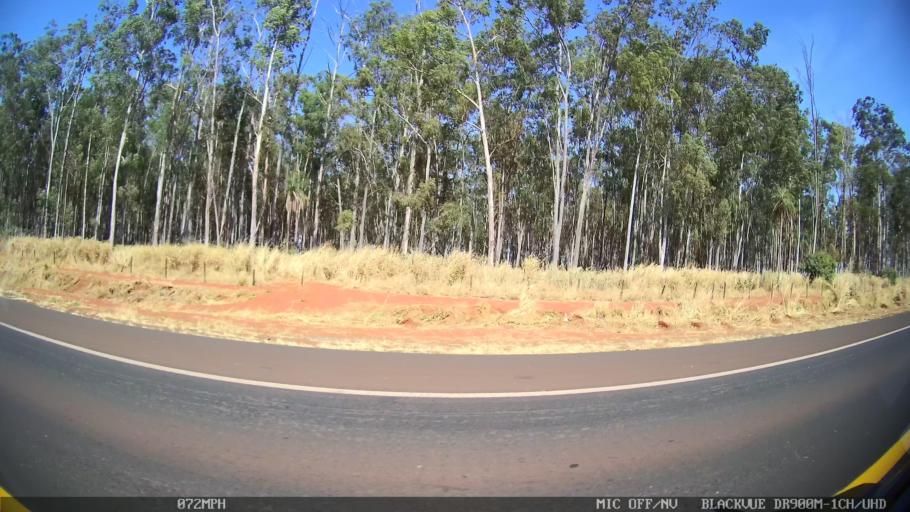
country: BR
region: Sao Paulo
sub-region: Barretos
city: Barretos
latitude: -20.4929
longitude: -48.5263
